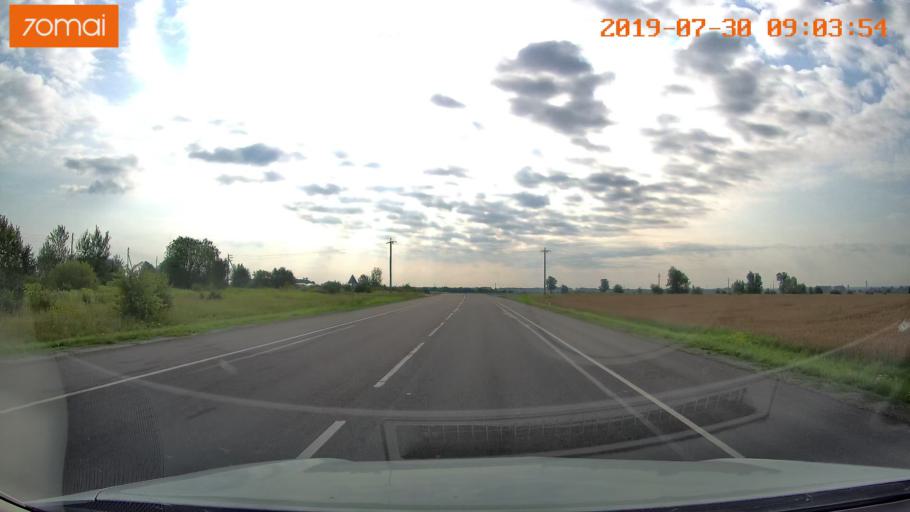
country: RU
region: Kaliningrad
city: Gusev
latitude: 54.6057
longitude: 22.2656
